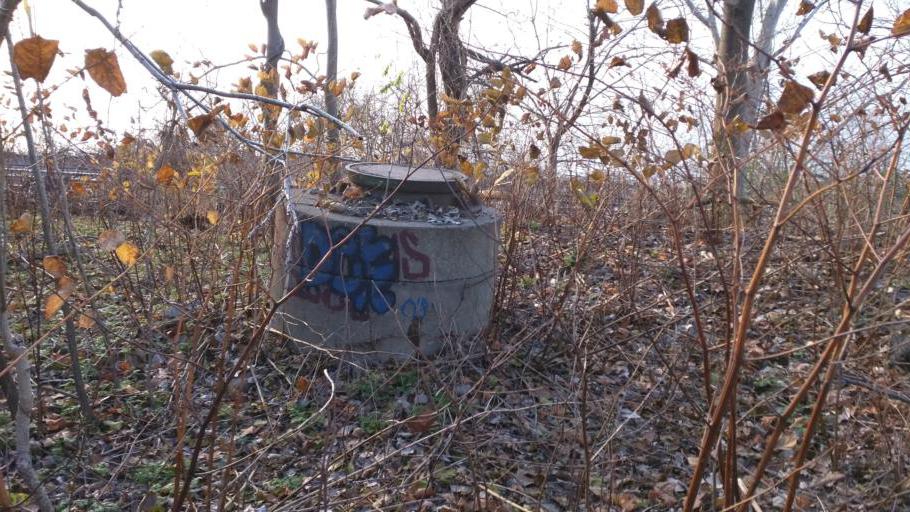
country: US
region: New York
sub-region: Westchester County
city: Hastings-on-Hudson
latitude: 40.9811
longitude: -73.8861
